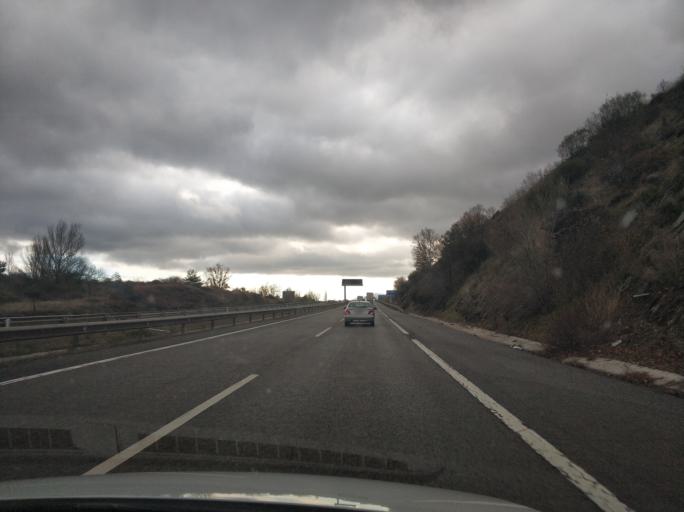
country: ES
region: Madrid
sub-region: Provincia de Madrid
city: Horcajo de la Sierra
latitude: 41.0746
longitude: -3.6046
